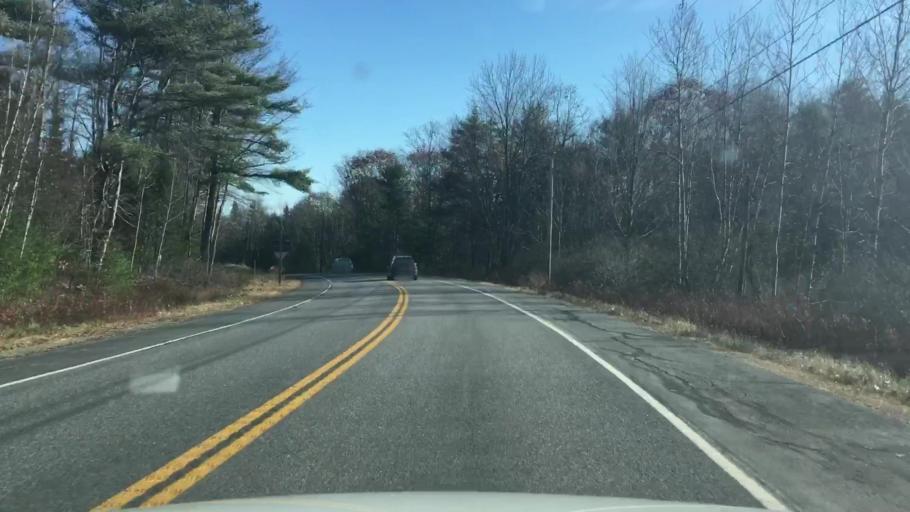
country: US
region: Maine
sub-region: Knox County
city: Washington
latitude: 44.2414
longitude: -69.3792
